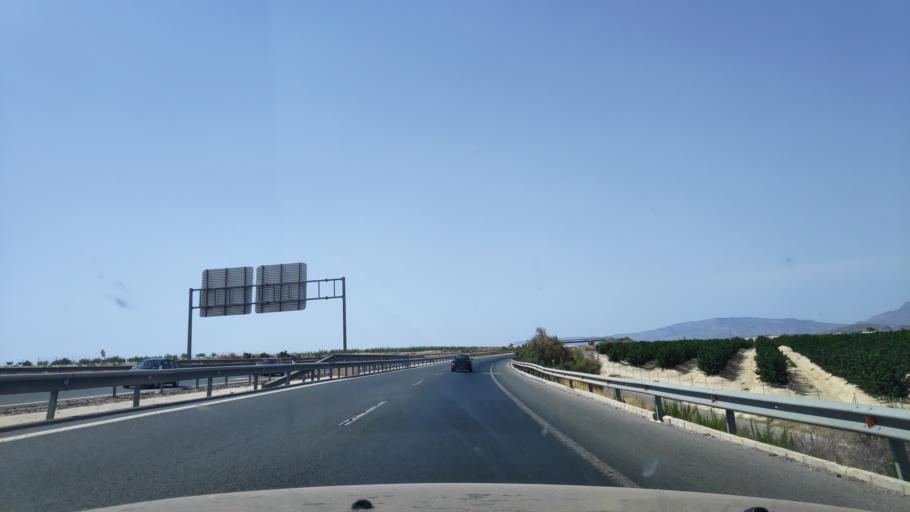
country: ES
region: Murcia
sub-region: Murcia
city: Lorqui
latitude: 38.1067
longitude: -1.2375
